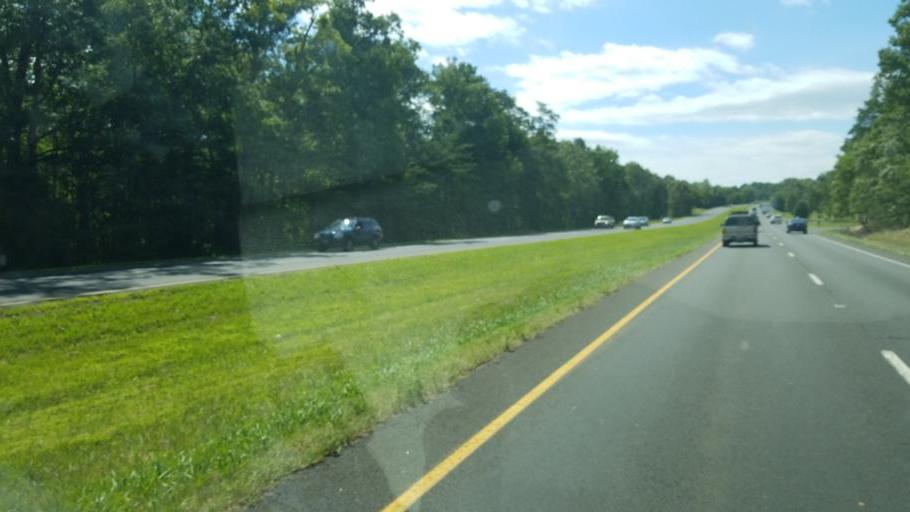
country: US
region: Virginia
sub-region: Fauquier County
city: Bealeton
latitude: 38.4886
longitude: -77.6835
